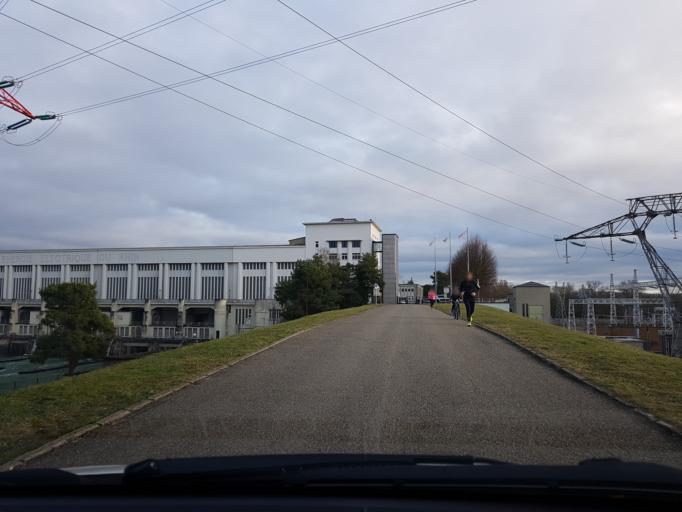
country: FR
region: Alsace
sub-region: Departement du Haut-Rhin
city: Rosenau
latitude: 47.6559
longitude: 7.5170
